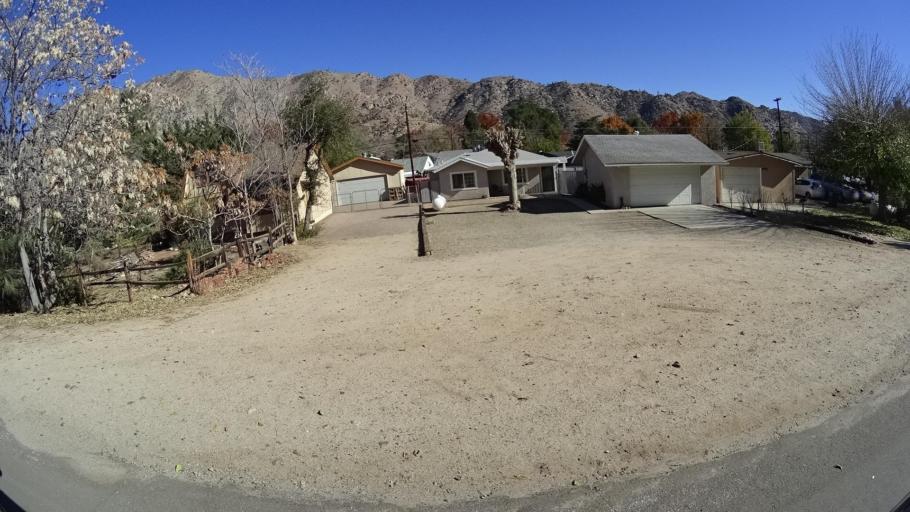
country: US
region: California
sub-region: Kern County
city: Kernville
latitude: 35.7568
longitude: -118.4287
